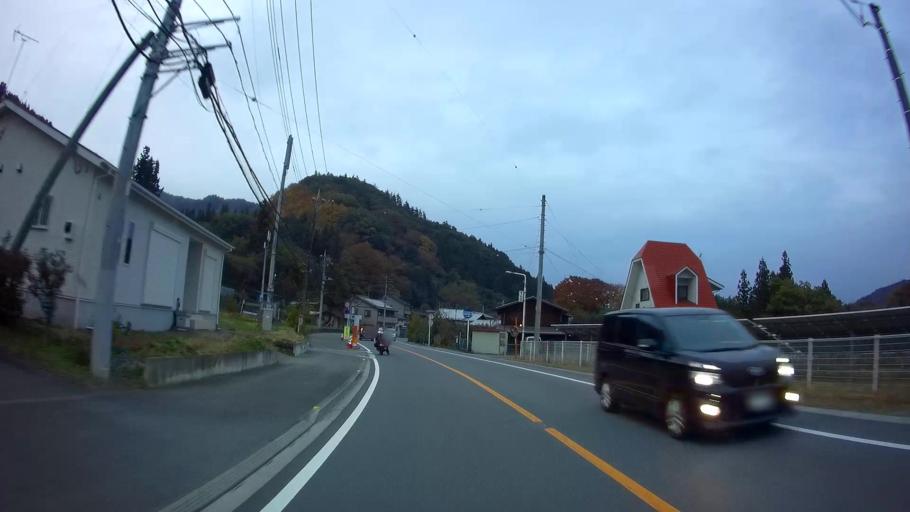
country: JP
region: Gunma
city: Nakanojomachi
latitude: 36.5601
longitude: 138.7667
